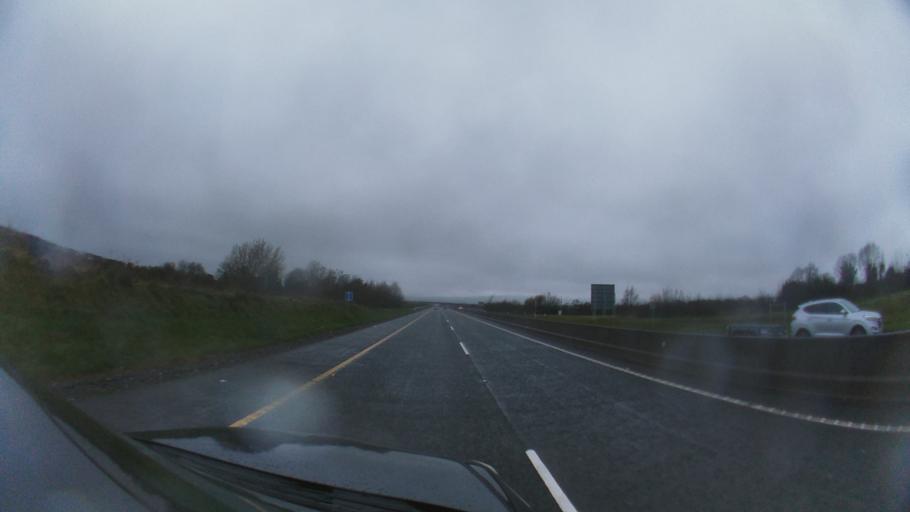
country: IE
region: Leinster
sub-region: County Carlow
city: Carlow
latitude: 52.7904
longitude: -6.9047
